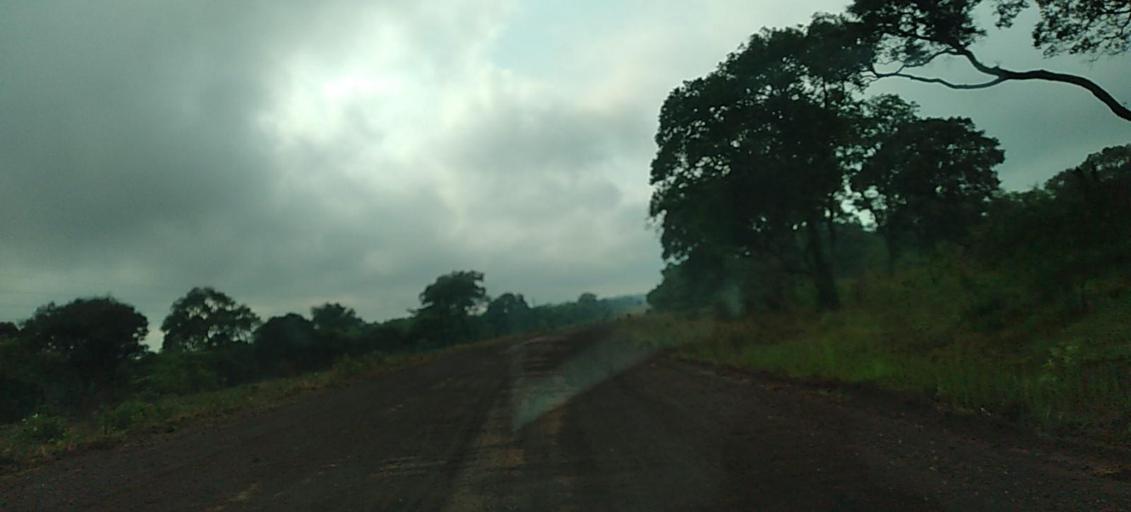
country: ZM
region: North-Western
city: Mwinilunga
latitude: -11.7265
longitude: 24.5771
